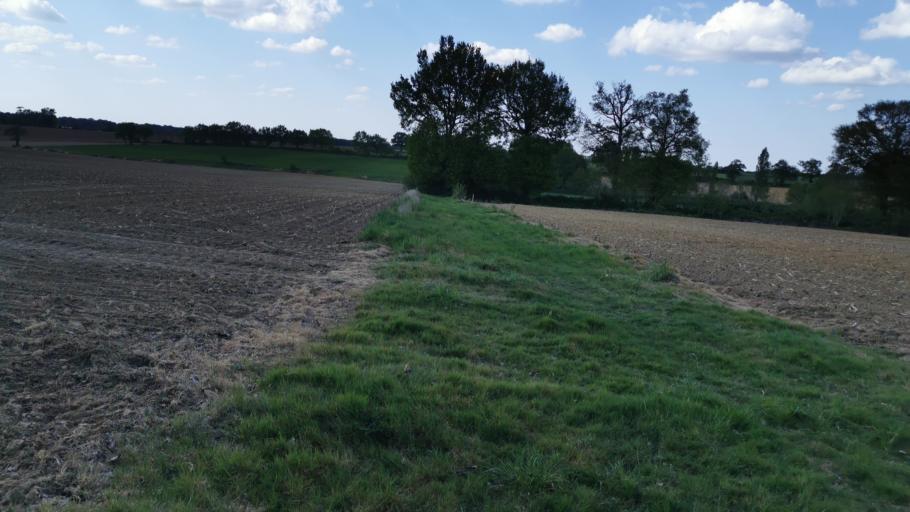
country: FR
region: Poitou-Charentes
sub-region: Departement de la Vienne
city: Availles-Limouzine
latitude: 46.1298
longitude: 0.5838
